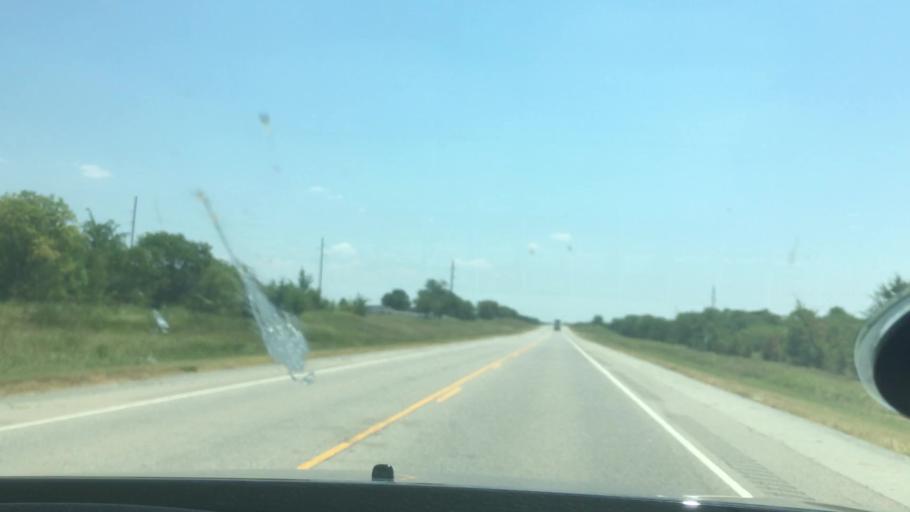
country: US
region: Oklahoma
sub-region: Pontotoc County
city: Ada
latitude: 34.6371
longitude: -96.4800
